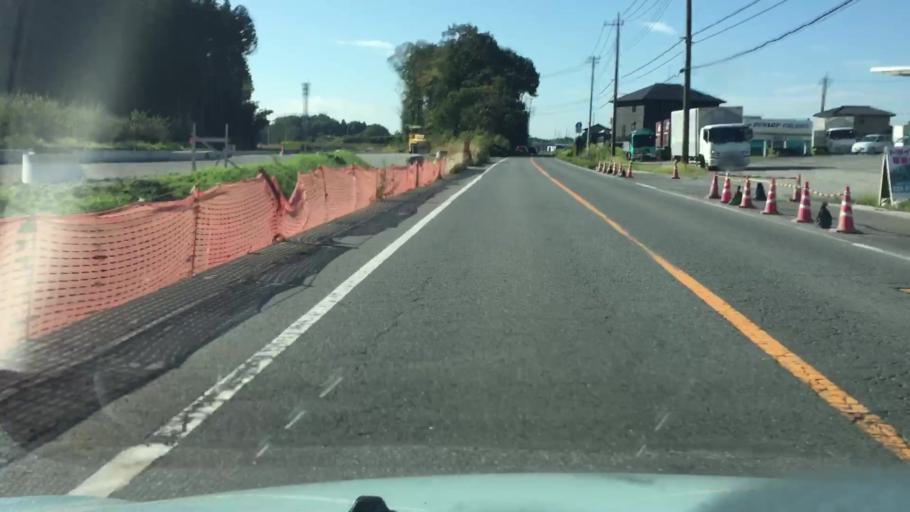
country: JP
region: Tochigi
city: Ujiie
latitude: 36.5868
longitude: 139.9835
